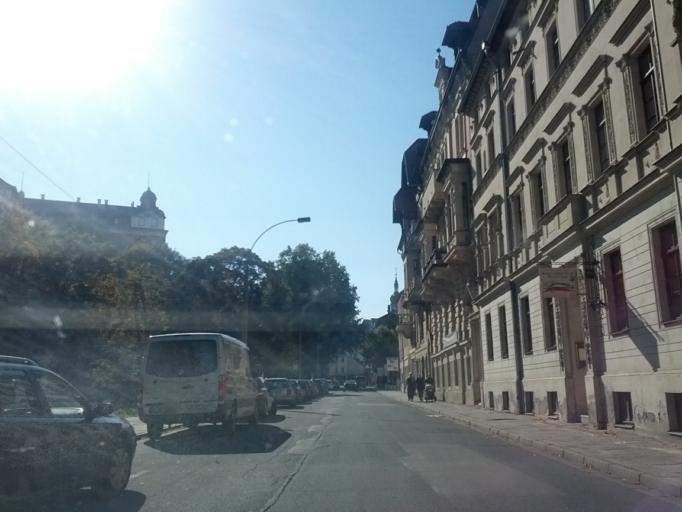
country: DE
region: Thuringia
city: Altenburg
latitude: 50.9900
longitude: 12.4392
